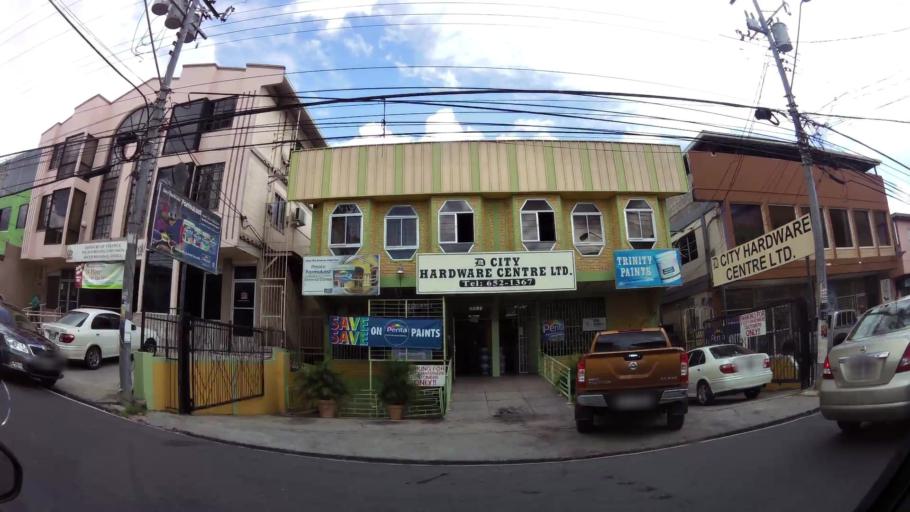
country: TT
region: City of San Fernando
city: San Fernando
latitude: 10.2697
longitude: -61.4598
